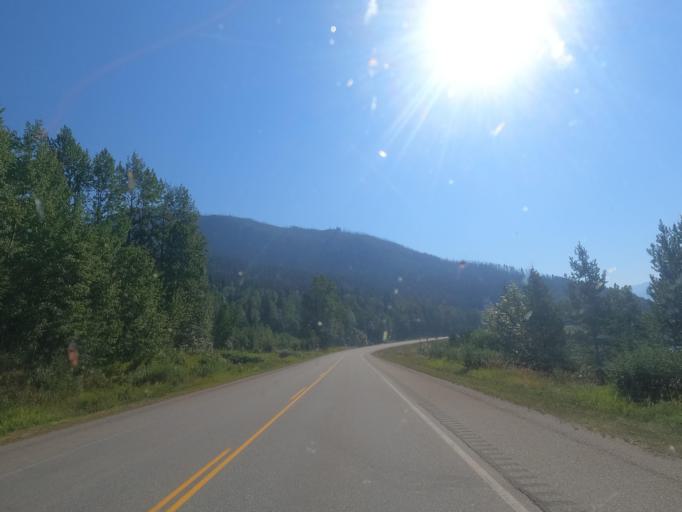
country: CA
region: Alberta
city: Jasper Park Lodge
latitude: 52.9525
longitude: -118.8702
